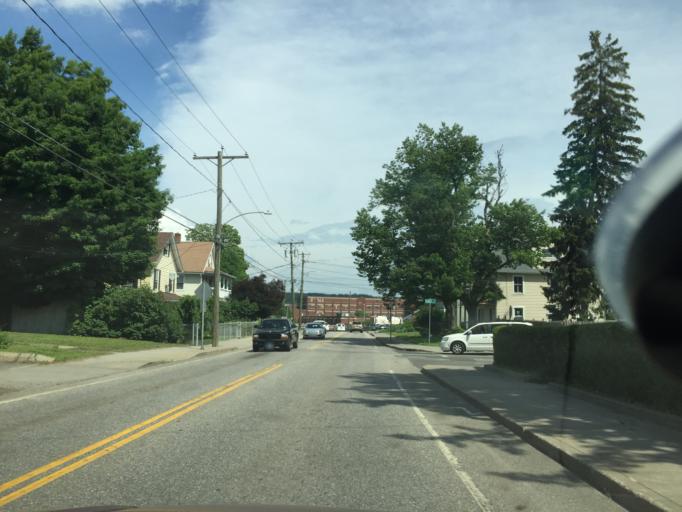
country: US
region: Connecticut
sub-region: Litchfield County
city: Torrington
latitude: 41.8123
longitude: -73.1277
